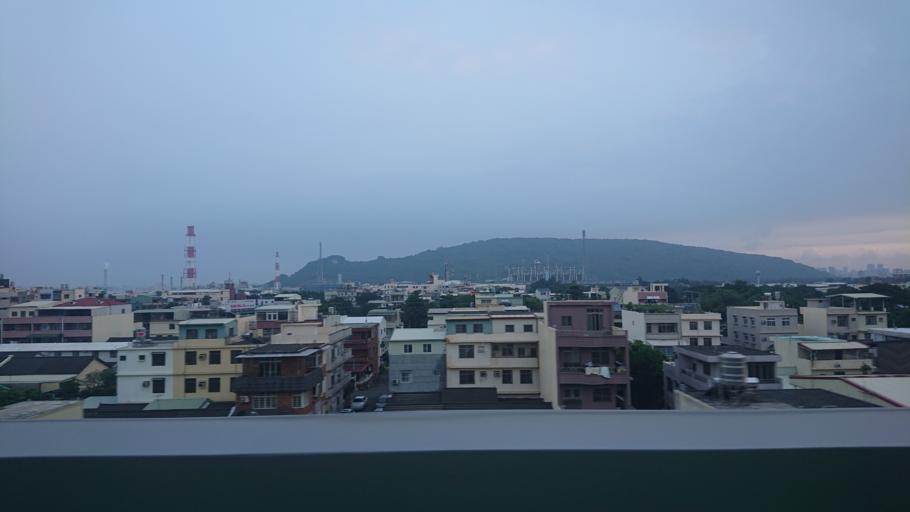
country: TW
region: Kaohsiung
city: Kaohsiung
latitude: 22.7187
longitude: 120.3079
